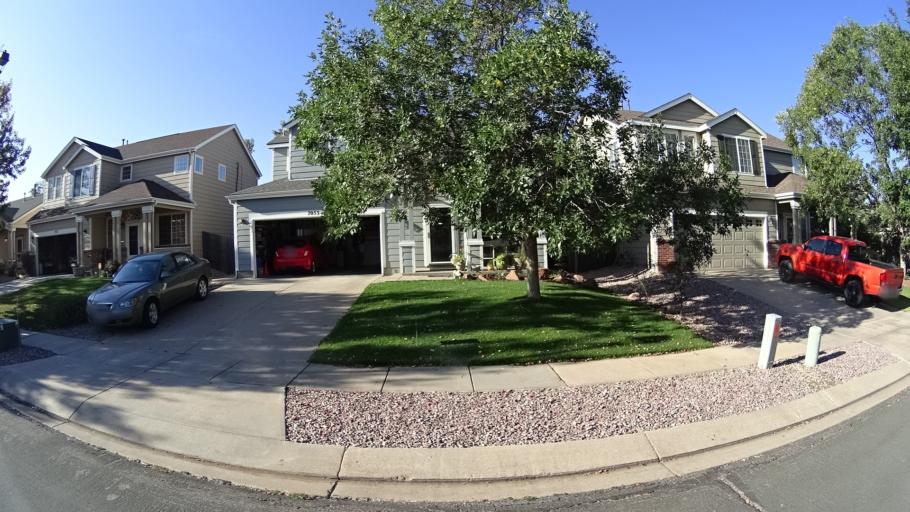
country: US
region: Colorado
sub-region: El Paso County
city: Cimarron Hills
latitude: 38.8833
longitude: -104.6957
